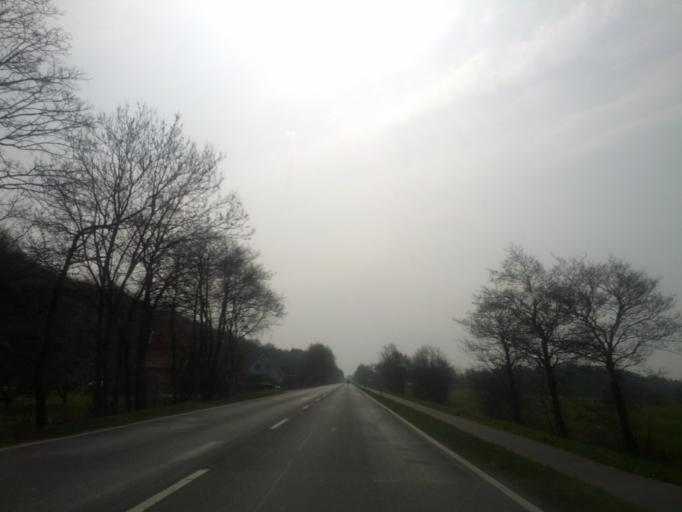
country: DE
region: Lower Saxony
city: Lutetsburg
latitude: 53.5778
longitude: 7.2336
